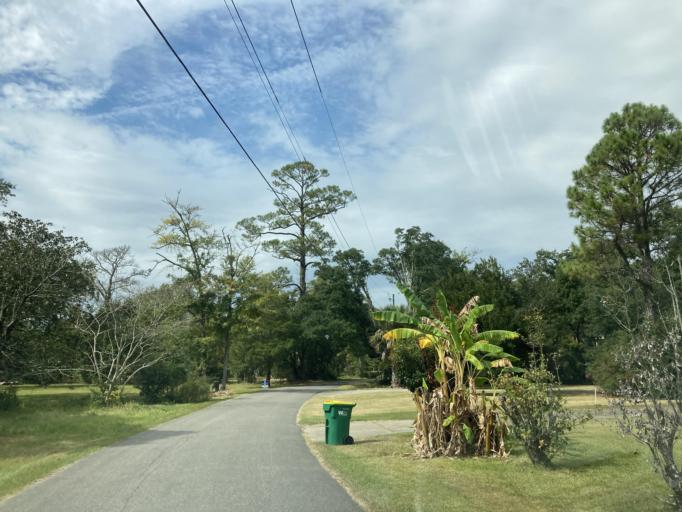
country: US
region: Mississippi
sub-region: Jackson County
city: Gulf Hills
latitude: 30.4304
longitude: -88.8423
